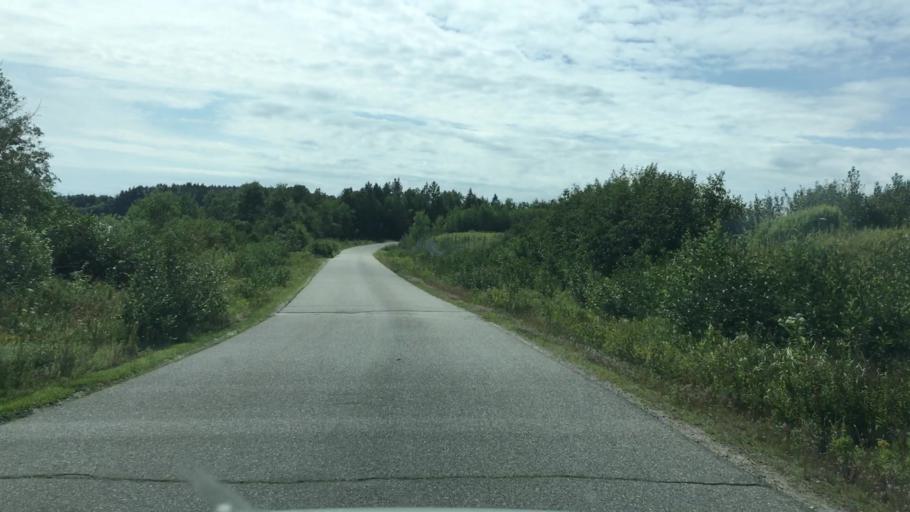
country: US
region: Maine
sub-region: Washington County
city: Eastport
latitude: 44.9067
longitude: -67.0039
